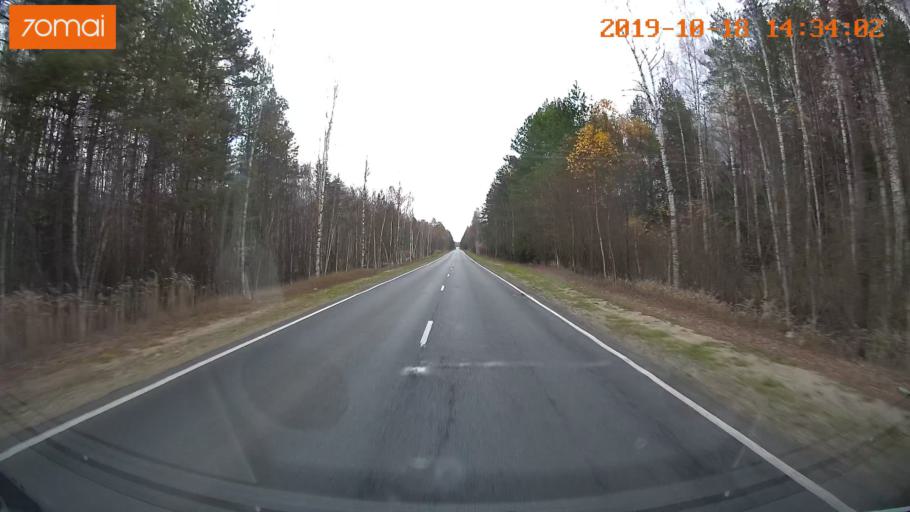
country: RU
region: Vladimir
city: Velikodvorskiy
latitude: 55.2079
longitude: 40.6083
